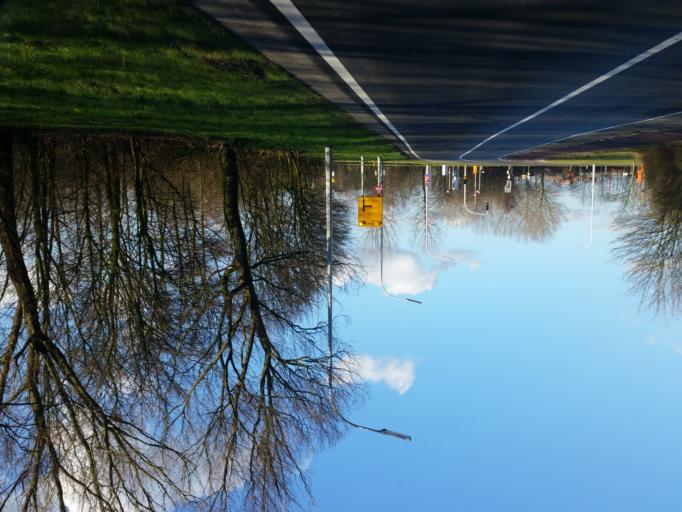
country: BE
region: Flanders
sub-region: Provincie Oost-Vlaanderen
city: Beveren
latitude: 51.2618
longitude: 4.2791
